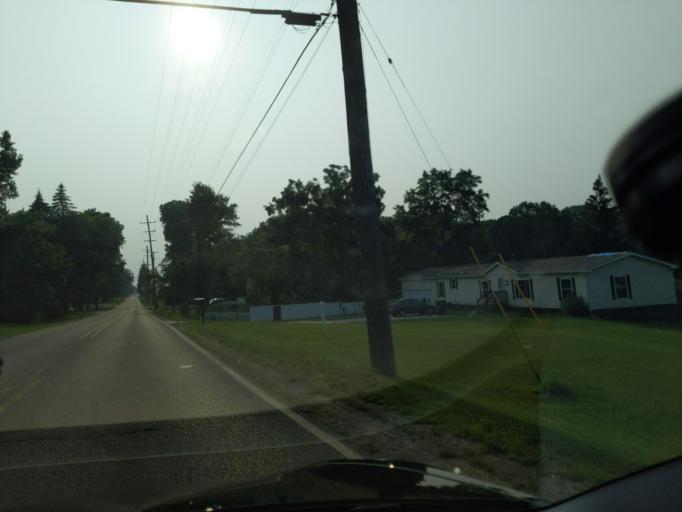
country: US
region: Michigan
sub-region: Jackson County
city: Jackson
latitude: 42.2620
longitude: -84.4380
